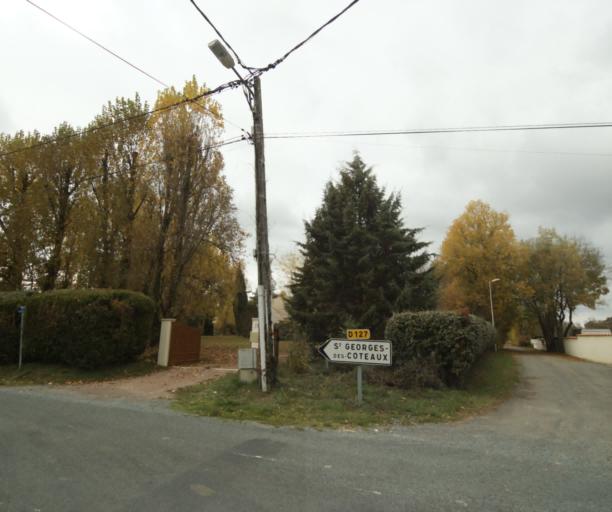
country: FR
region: Poitou-Charentes
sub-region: Departement de la Charente-Maritime
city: Saint-Georges-des-Coteaux
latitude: 45.7810
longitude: -0.6992
